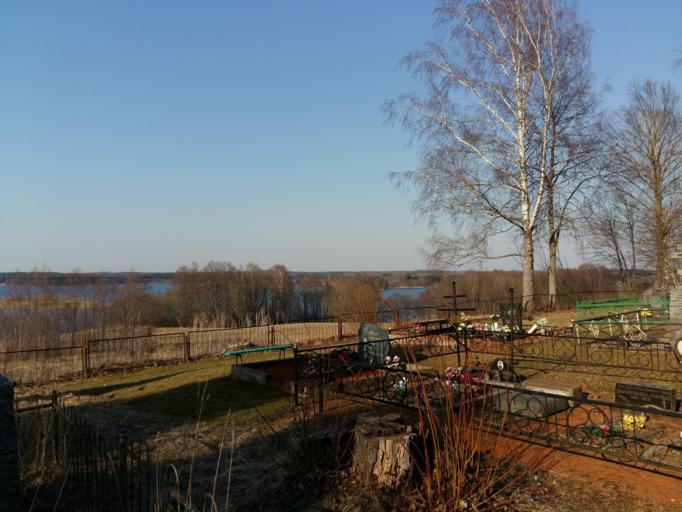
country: LT
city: Zarasai
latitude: 55.5975
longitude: 26.0292
